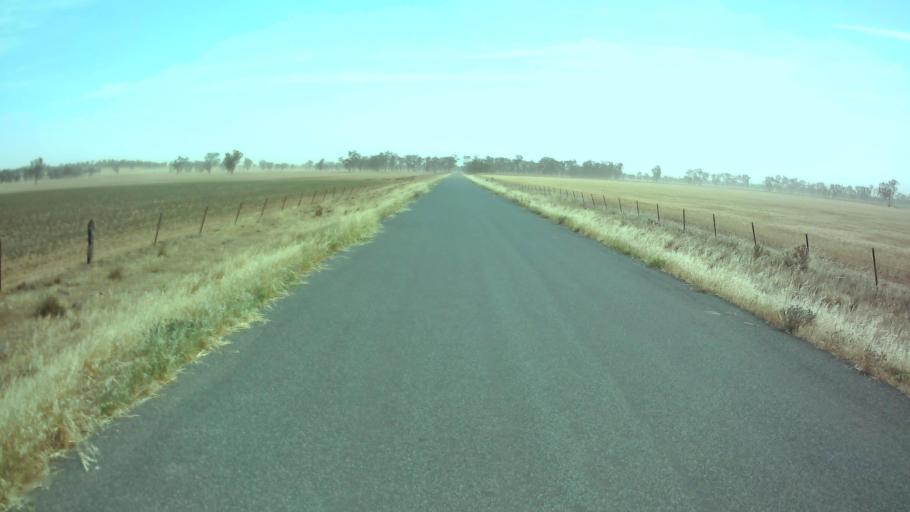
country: AU
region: New South Wales
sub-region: Weddin
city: Grenfell
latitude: -33.7244
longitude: 147.9992
